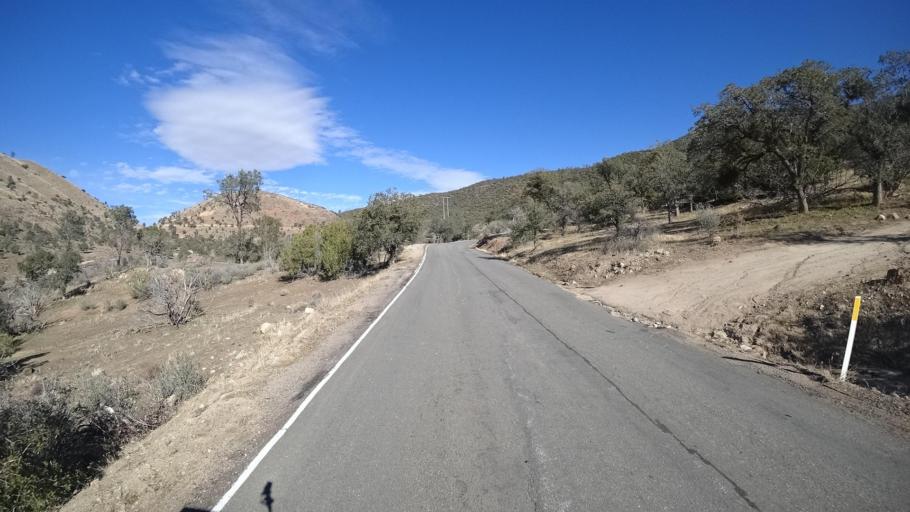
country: US
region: California
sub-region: Kern County
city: Bodfish
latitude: 35.5603
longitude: -118.5075
